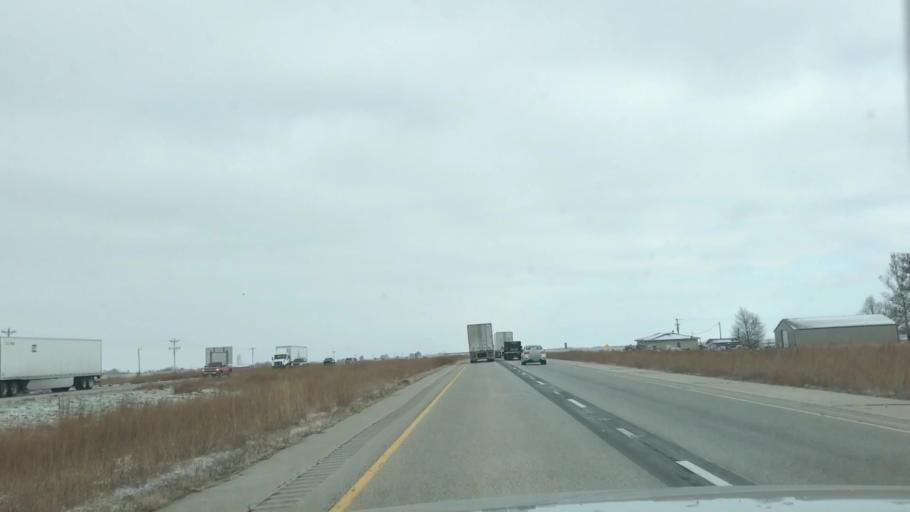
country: US
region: Illinois
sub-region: Sangamon County
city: Divernon
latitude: 39.4634
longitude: -89.6443
